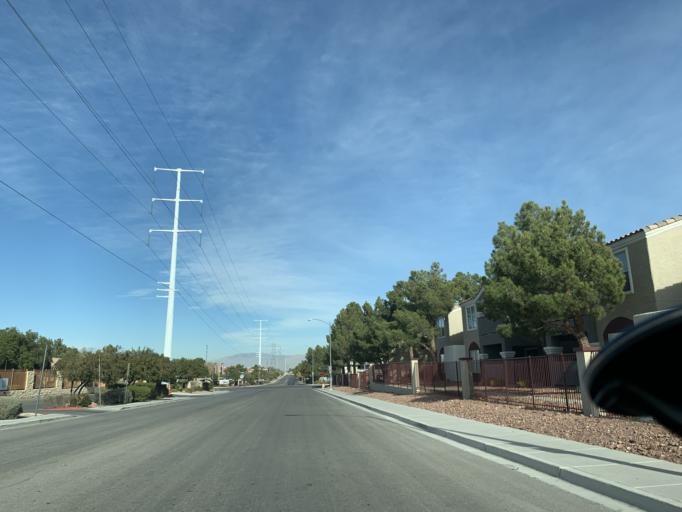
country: US
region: Nevada
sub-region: Clark County
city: Spring Valley
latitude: 36.0923
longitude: -115.2122
